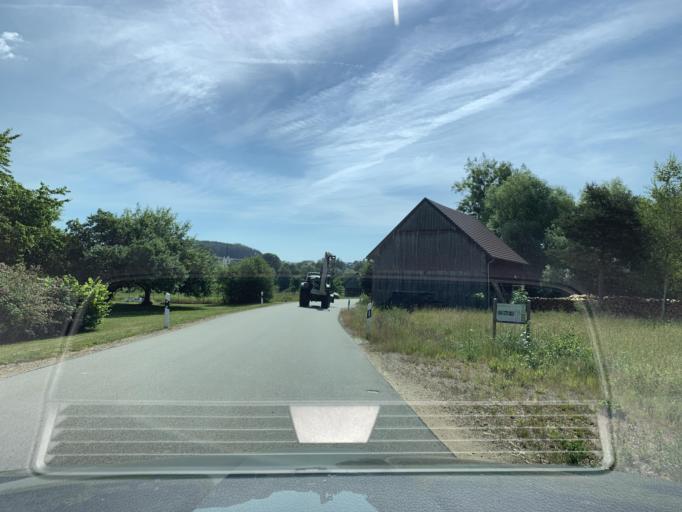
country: DE
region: Bavaria
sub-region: Upper Palatinate
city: Schwarzhofen
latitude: 49.3776
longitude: 12.3349
